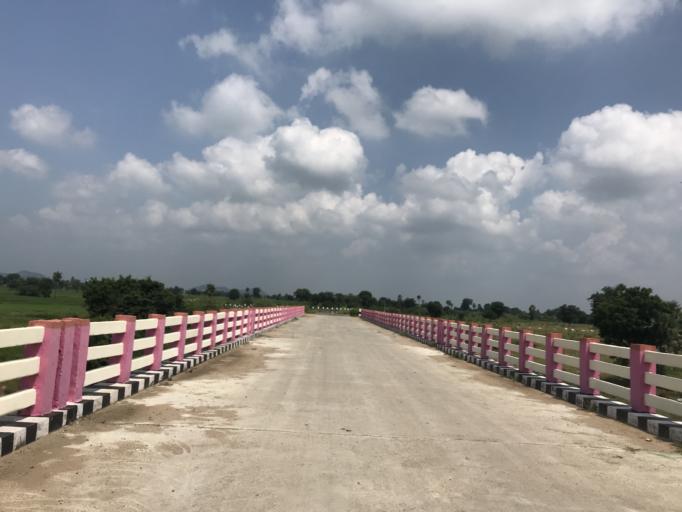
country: IN
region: Telangana
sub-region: Warangal
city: Mahbubabad
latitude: 17.6853
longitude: 79.7139
